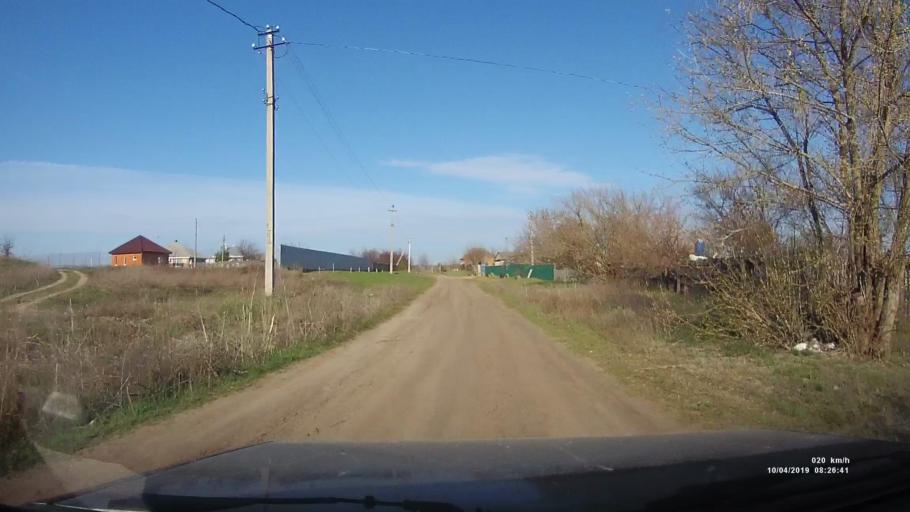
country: RU
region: Rostov
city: Kamensk-Shakhtinskiy
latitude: 48.3582
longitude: 40.2270
